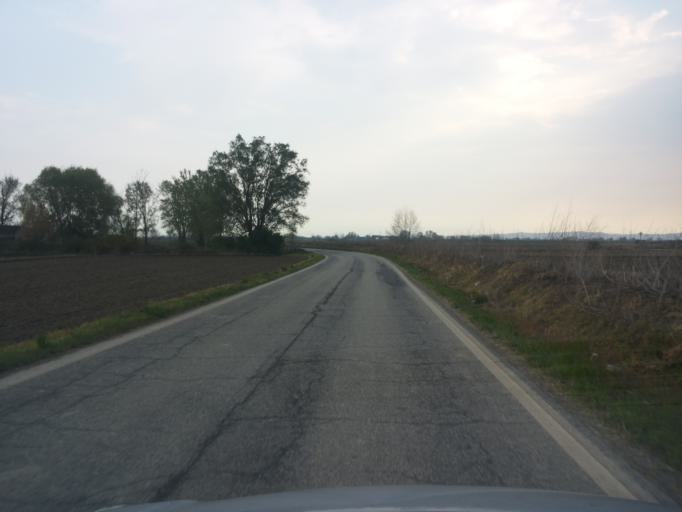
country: IT
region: Piedmont
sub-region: Provincia di Vercelli
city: Caresana
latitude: 45.2040
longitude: 8.4976
